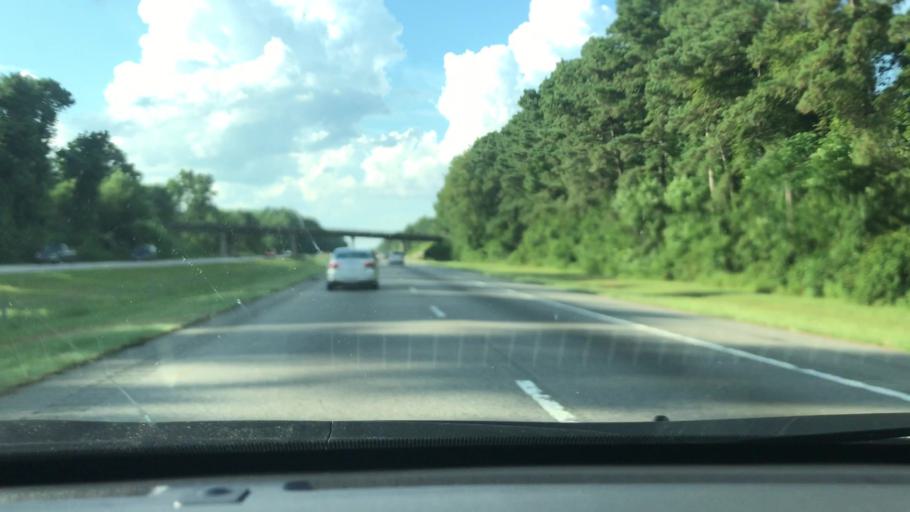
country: US
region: North Carolina
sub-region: Robeson County
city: Saint Pauls
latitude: 34.7680
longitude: -78.9963
